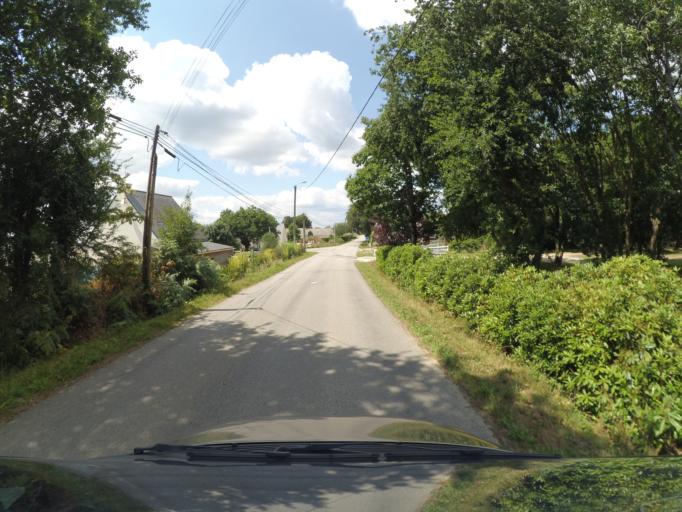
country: FR
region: Brittany
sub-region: Departement du Morbihan
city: Landaul
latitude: 47.7415
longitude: -3.0633
